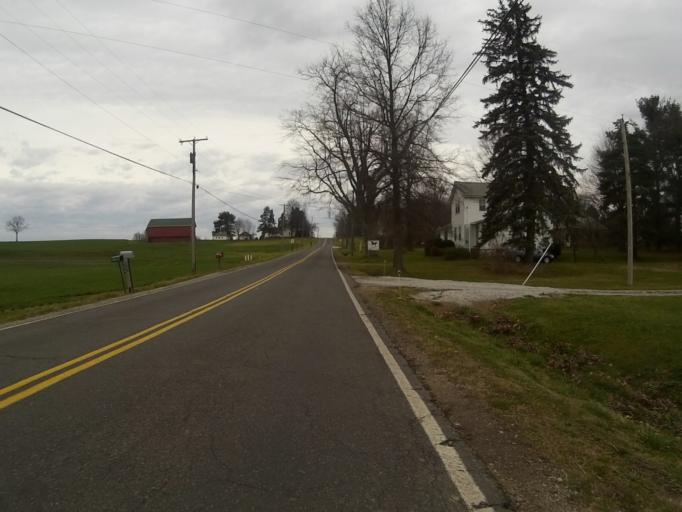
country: US
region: Ohio
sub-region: Stark County
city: Hartville
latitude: 41.0080
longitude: -81.3294
